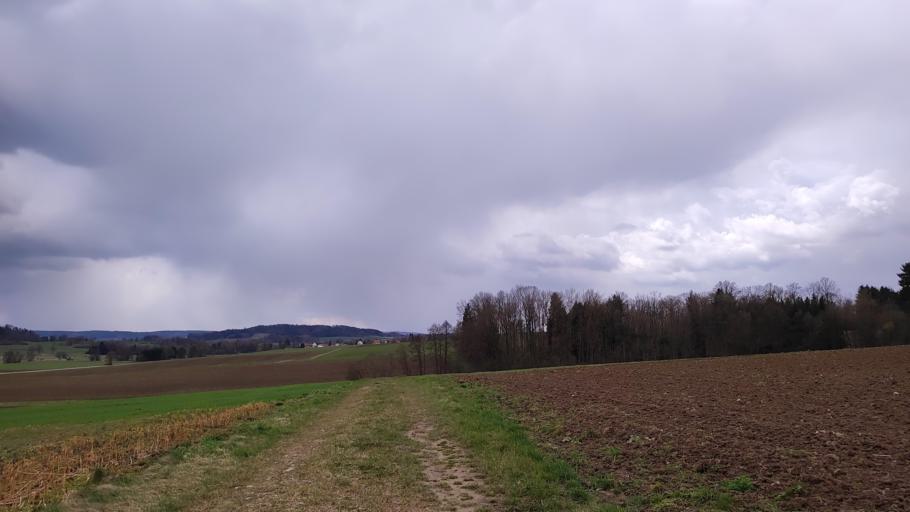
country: DE
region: Bavaria
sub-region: Swabia
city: Dinkelscherben
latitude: 48.3743
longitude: 10.5684
